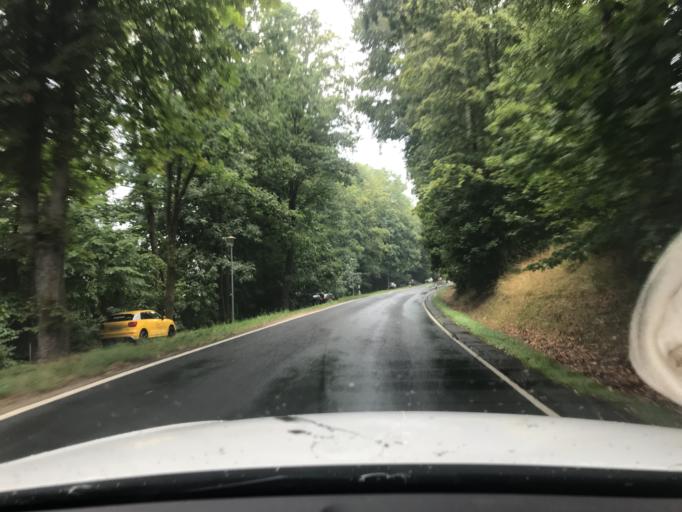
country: DE
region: Bavaria
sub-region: Upper Palatinate
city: Speinshart
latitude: 49.7564
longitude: 11.8093
